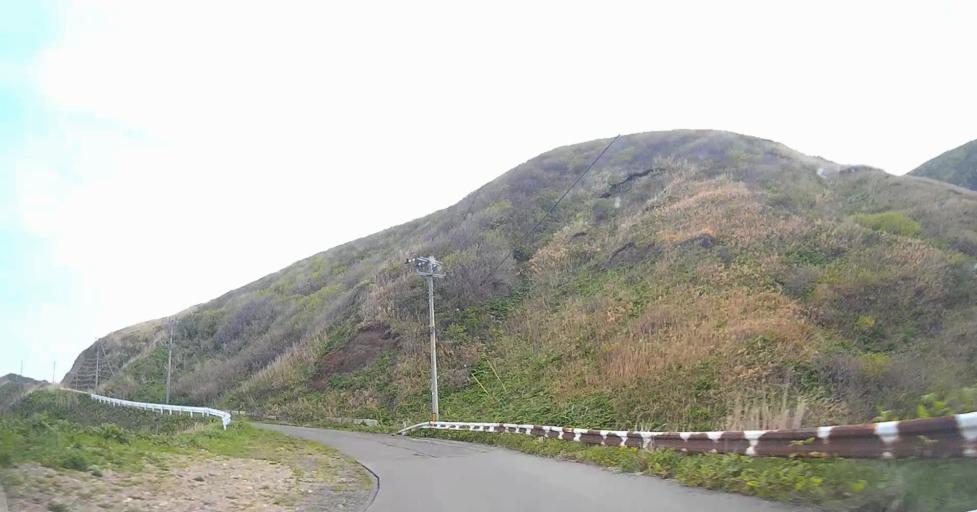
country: JP
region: Aomori
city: Shimokizukuri
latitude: 41.2469
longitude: 140.3437
